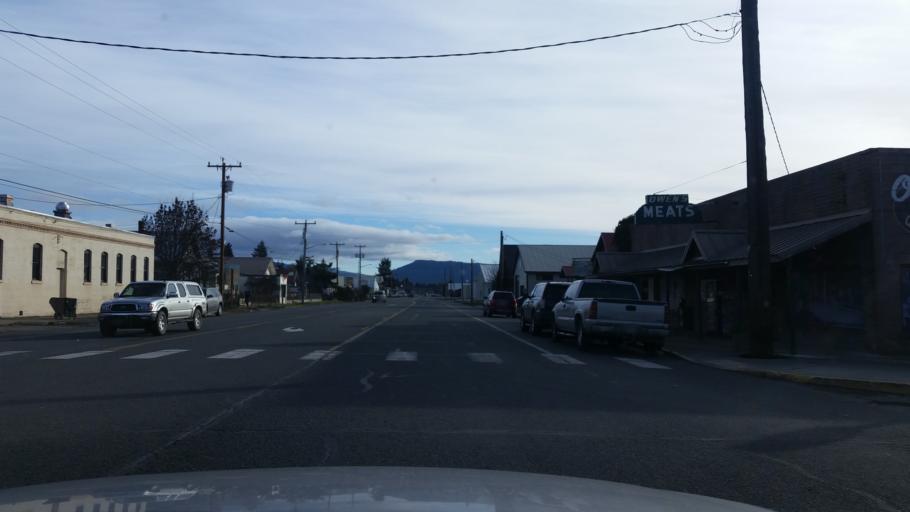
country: US
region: Washington
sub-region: Kittitas County
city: Cle Elum
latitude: 47.1940
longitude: -120.9313
